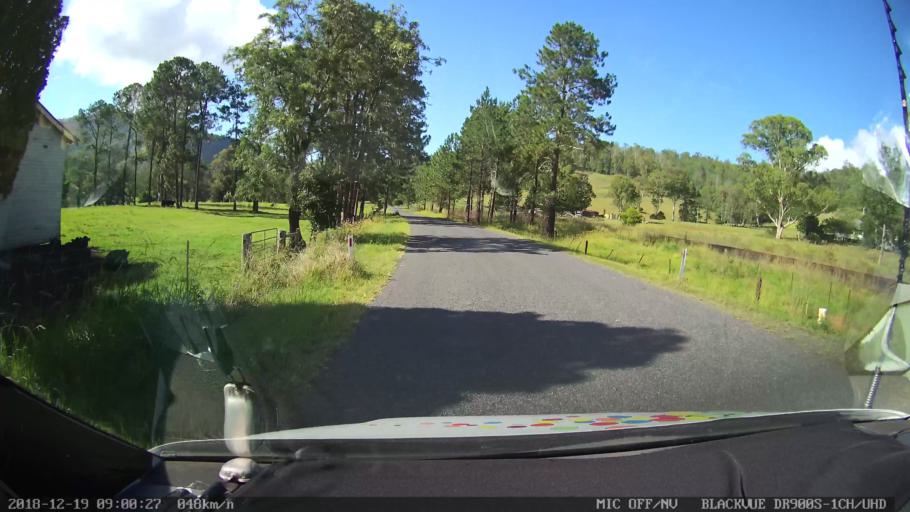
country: AU
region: New South Wales
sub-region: Kyogle
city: Kyogle
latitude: -28.4319
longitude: 152.9571
